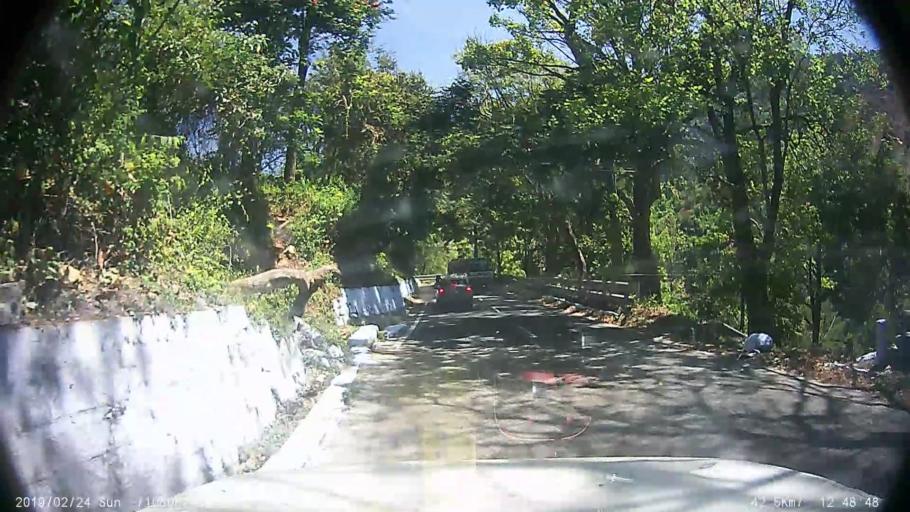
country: IN
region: Tamil Nadu
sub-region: Nilgiri
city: Wellington
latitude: 11.3298
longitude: 76.8032
